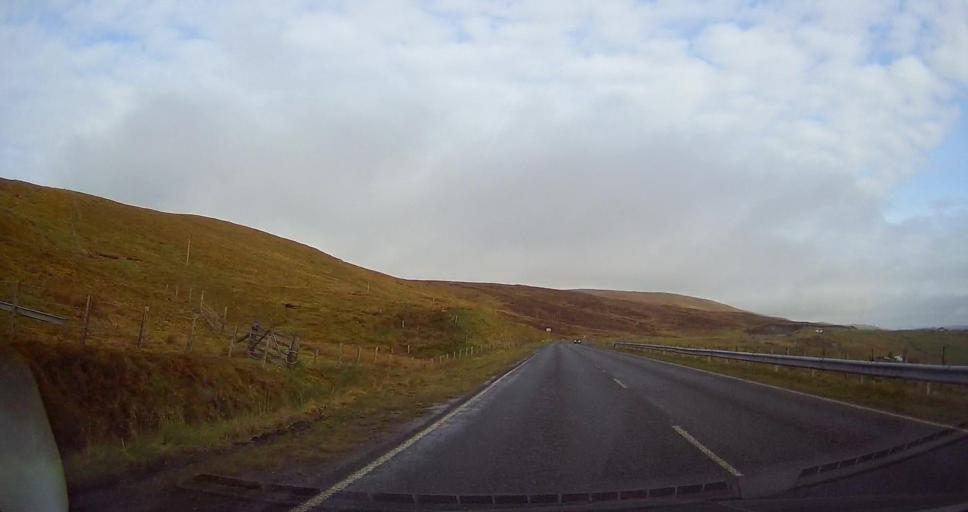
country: GB
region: Scotland
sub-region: Shetland Islands
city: Sandwick
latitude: 60.0692
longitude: -1.2273
